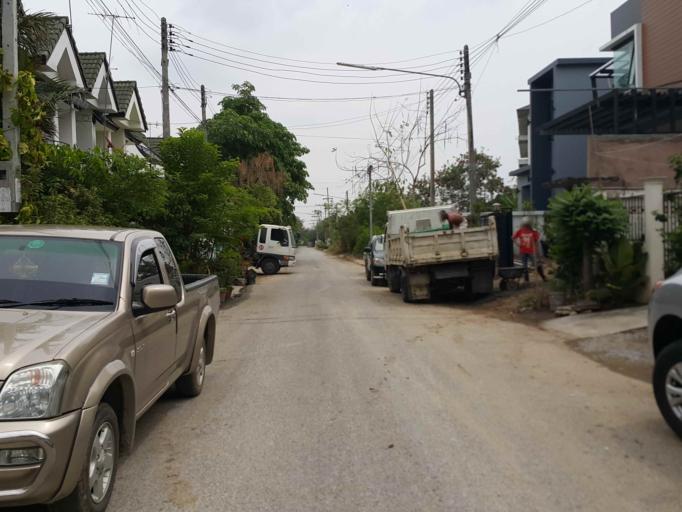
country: TH
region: Chiang Mai
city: Chiang Mai
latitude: 18.7587
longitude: 99.0179
